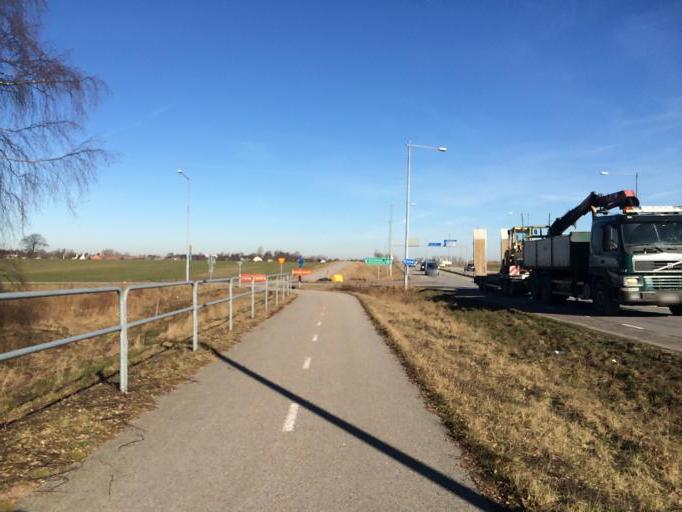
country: SE
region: Skane
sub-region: Kavlinge Kommun
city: Loddekopinge
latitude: 55.7465
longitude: 13.0284
